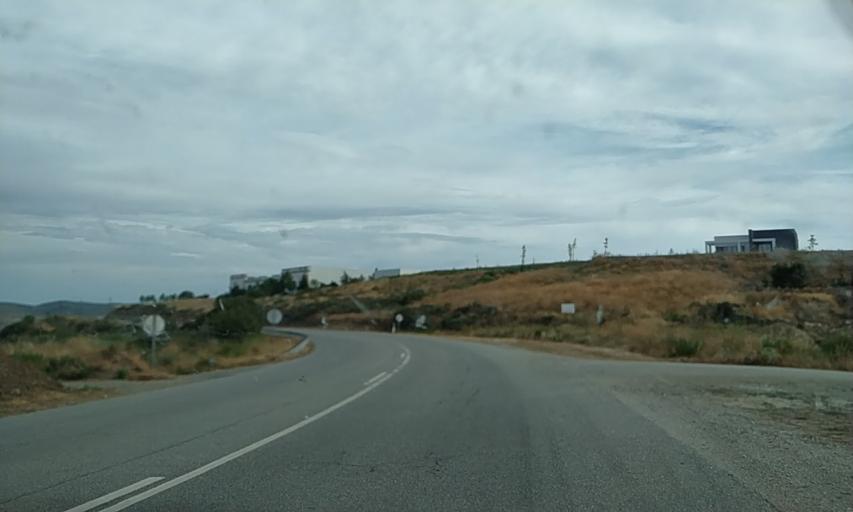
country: PT
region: Viseu
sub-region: Sao Joao da Pesqueira
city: Sao Joao da Pesqueira
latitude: 41.1197
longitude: -7.3901
